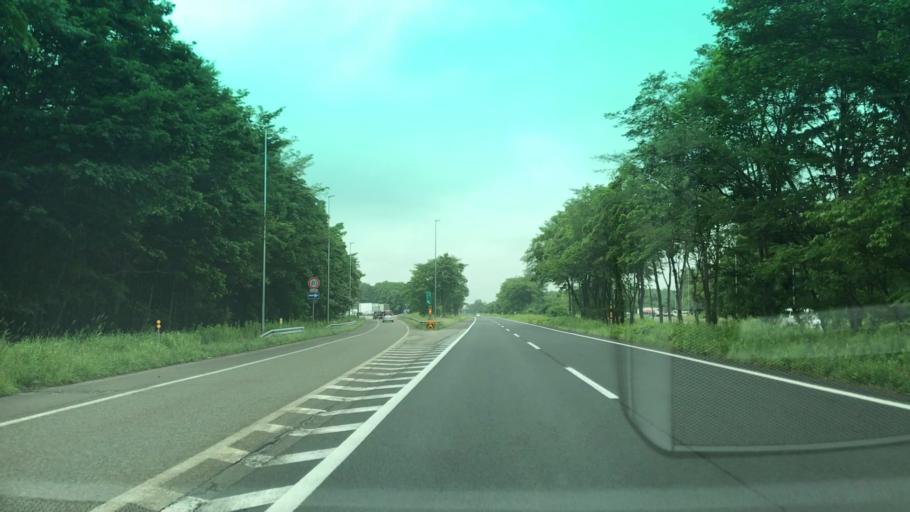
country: JP
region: Hokkaido
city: Chitose
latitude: 42.7544
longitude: 141.6433
